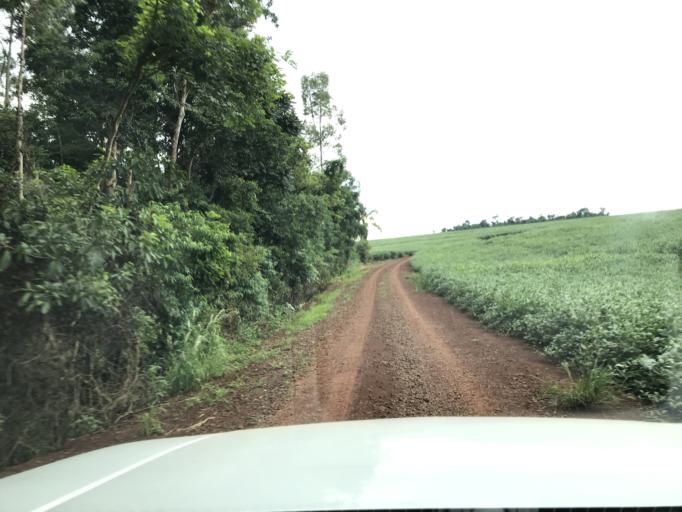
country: BR
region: Parana
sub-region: Palotina
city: Palotina
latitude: -24.2714
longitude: -53.7764
